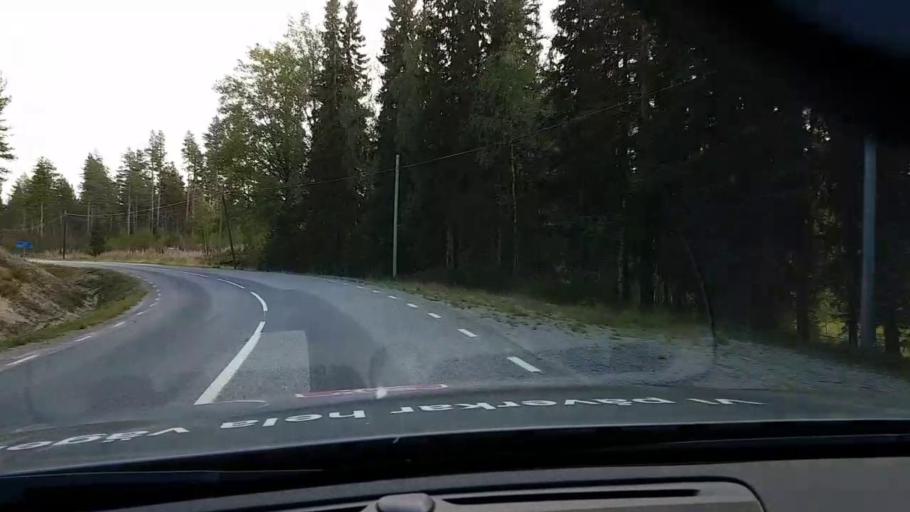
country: SE
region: Vaesterbotten
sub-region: Asele Kommun
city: Asele
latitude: 63.7949
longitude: 17.5673
